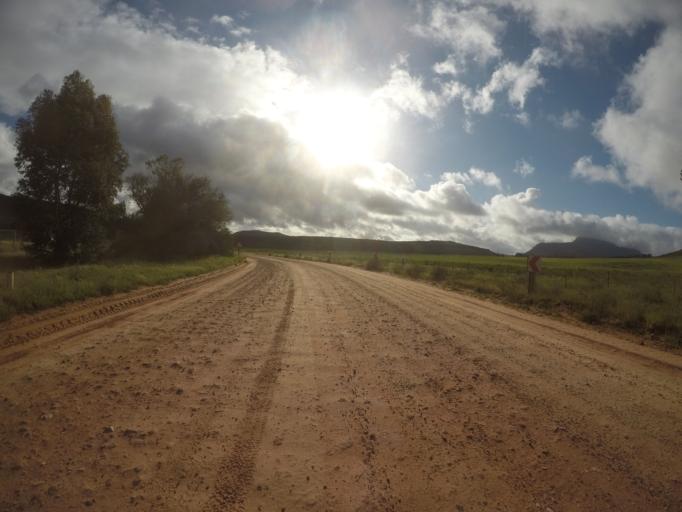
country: ZA
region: Western Cape
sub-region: West Coast District Municipality
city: Clanwilliam
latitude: -32.3435
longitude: 18.8357
